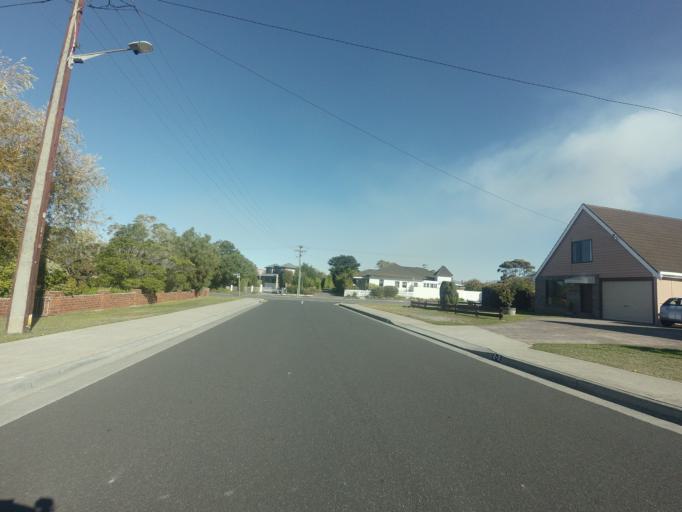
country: AU
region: Tasmania
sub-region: Clarence
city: Lindisfarne
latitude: -42.8491
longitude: 147.3466
